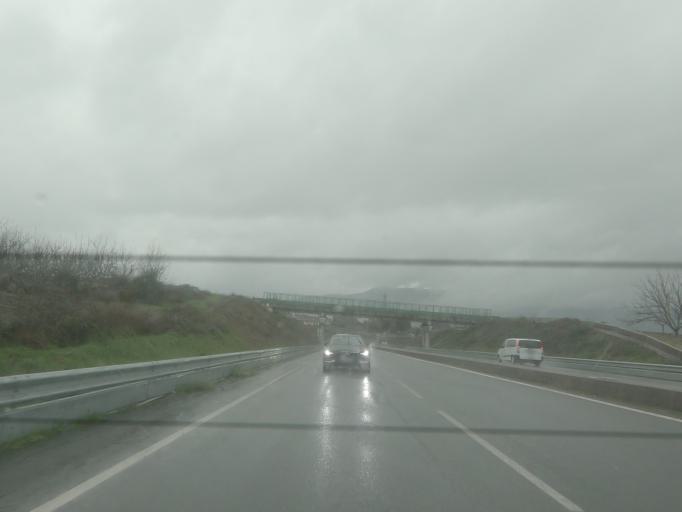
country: PT
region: Vila Real
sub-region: Vila Real
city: Vila Real
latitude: 41.2849
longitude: -7.7292
